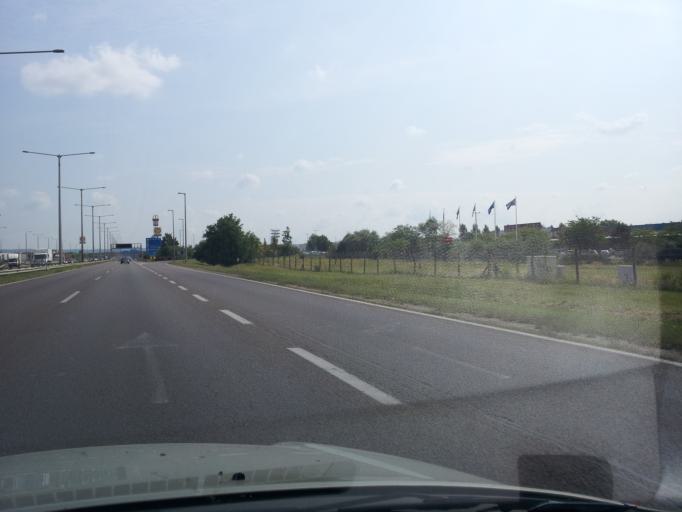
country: HU
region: Budapest
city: Budapest XV. keruelet
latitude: 47.5643
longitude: 19.1426
